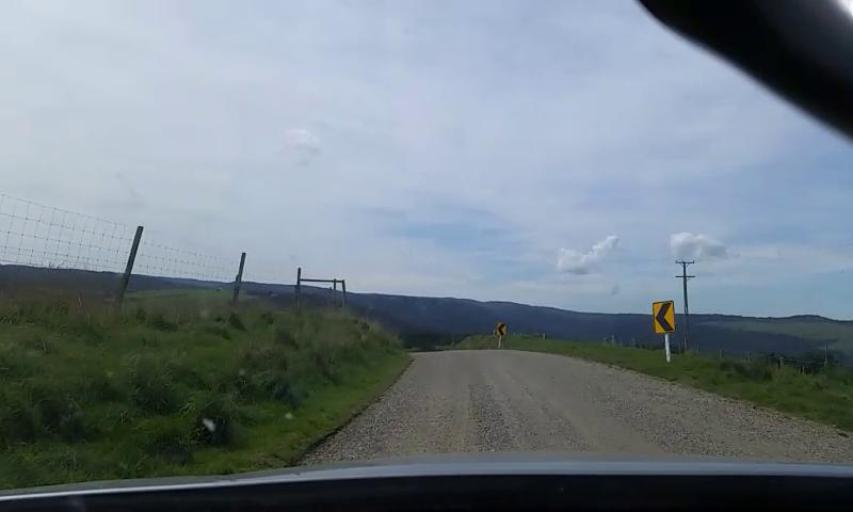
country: NZ
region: Otago
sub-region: Clutha District
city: Papatowai
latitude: -46.6307
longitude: 168.9816
